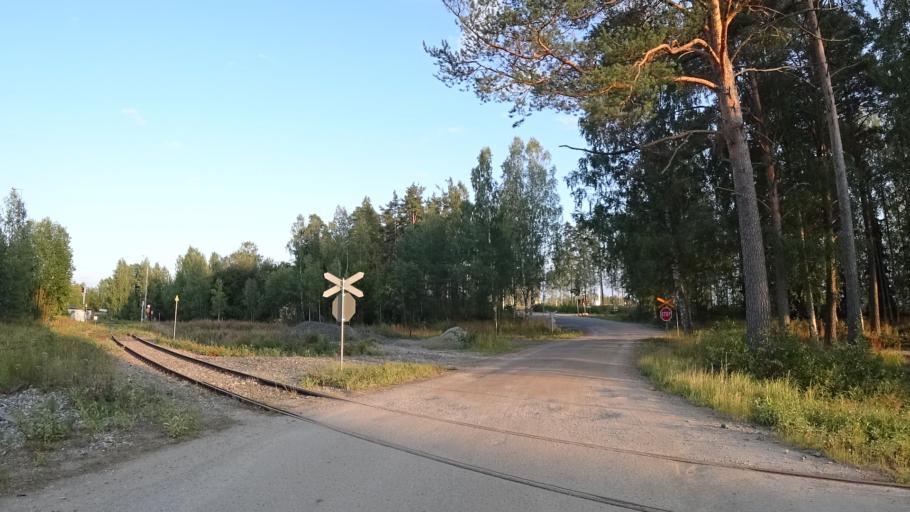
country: FI
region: Southern Savonia
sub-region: Savonlinna
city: Punkaharju
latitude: 61.7595
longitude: 29.3841
